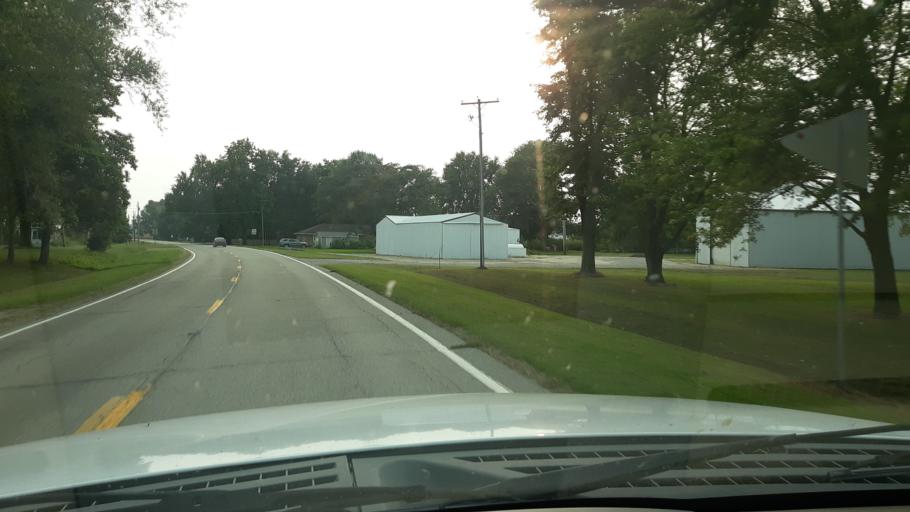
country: US
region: Illinois
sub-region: Edwards County
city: Grayville
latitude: 38.3131
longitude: -87.9359
